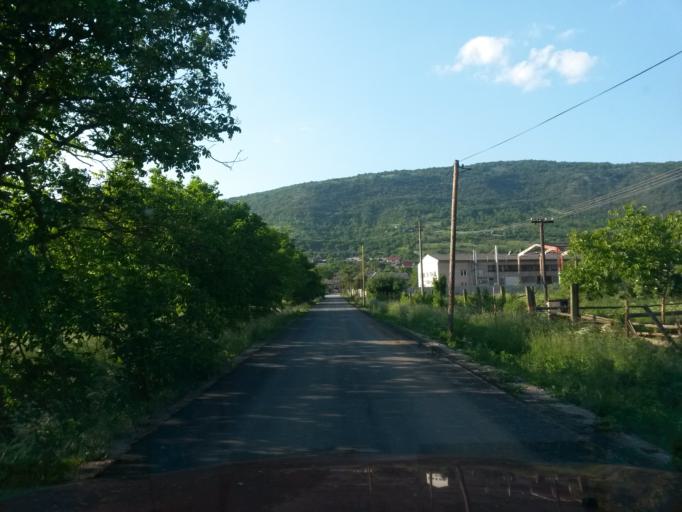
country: SK
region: Kosicky
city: Roznava
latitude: 48.5888
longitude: 20.6741
